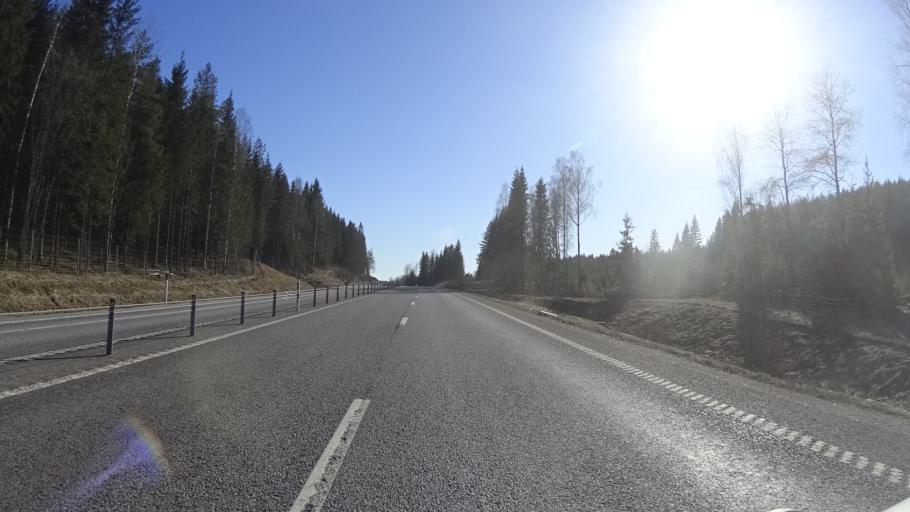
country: SE
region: Vaermland
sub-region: Arvika Kommun
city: Arvika
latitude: 59.6553
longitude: 12.7565
